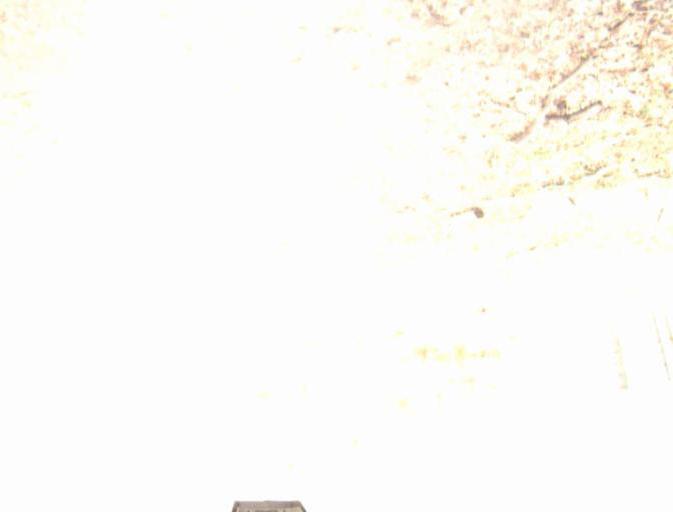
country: AU
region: Tasmania
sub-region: Dorset
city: Scottsdale
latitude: -41.4535
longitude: 147.6012
